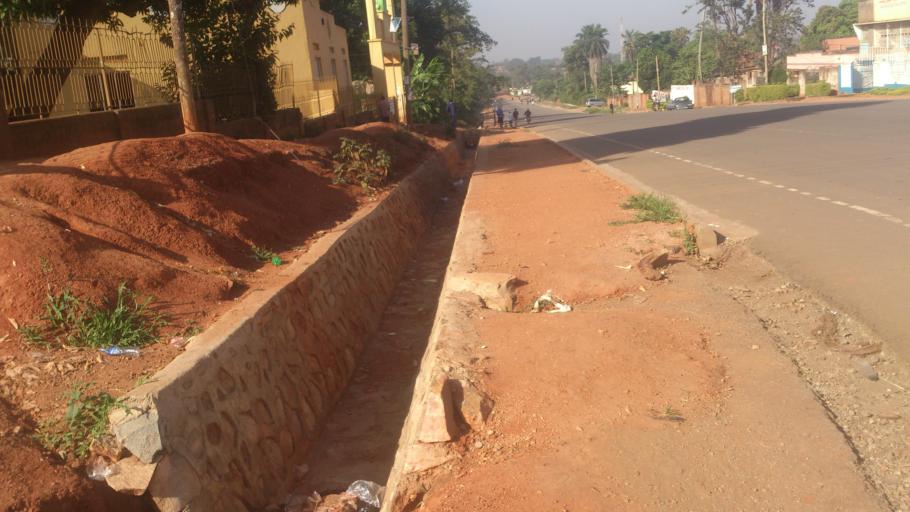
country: UG
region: Eastern Region
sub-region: Mbale District
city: Mbale
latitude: 1.0778
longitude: 34.1733
